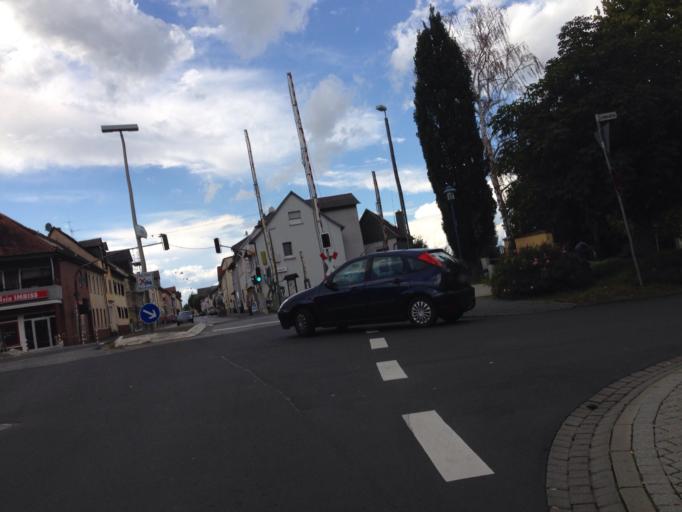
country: DE
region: Hesse
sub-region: Regierungsbezirk Giessen
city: Hungen
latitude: 50.4756
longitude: 8.8985
